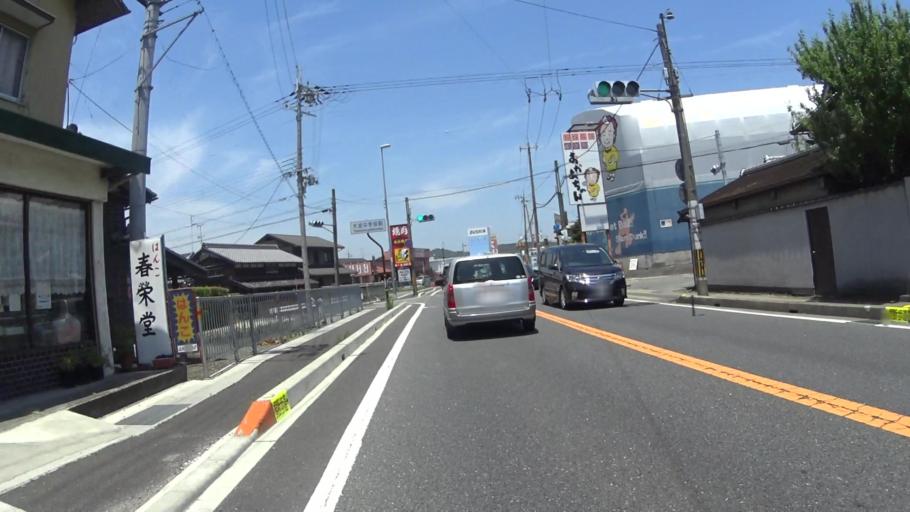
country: JP
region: Kyoto
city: Kameoka
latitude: 35.0388
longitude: 135.5473
